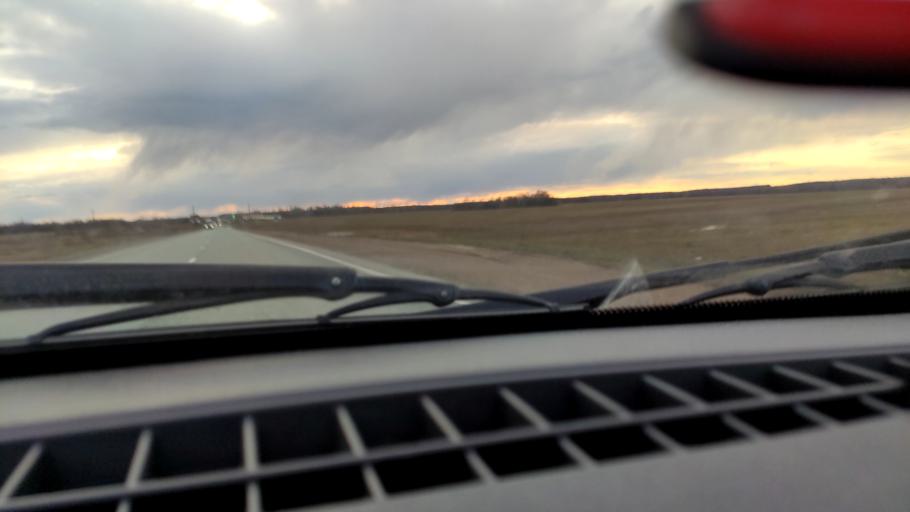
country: RU
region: Bashkortostan
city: Kudeyevskiy
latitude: 54.8169
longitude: 56.7514
